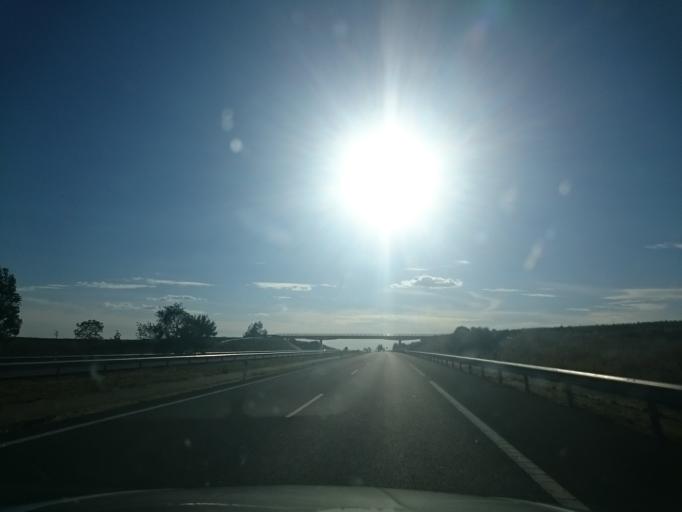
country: ES
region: Castille and Leon
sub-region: Provincia de Burgos
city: Grijalba
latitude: 42.3990
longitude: -4.1264
